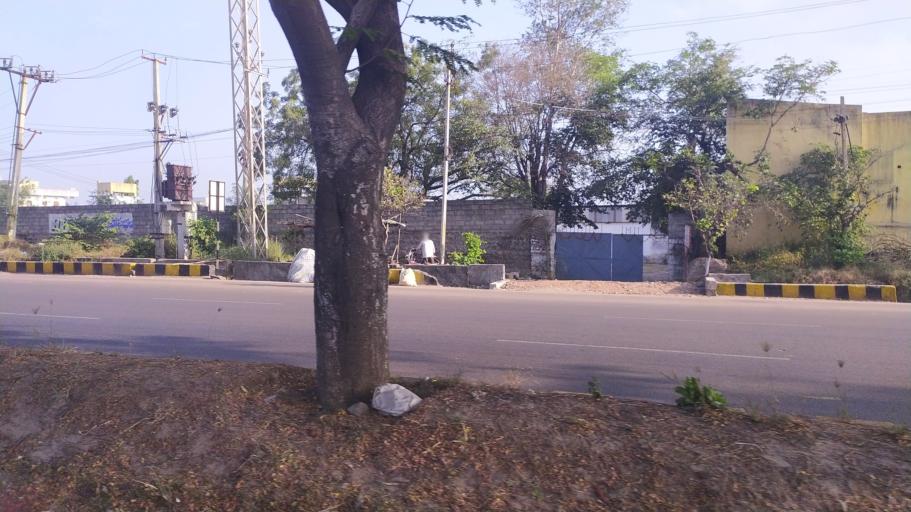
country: IN
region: Telangana
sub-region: Rangareddi
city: Balapur
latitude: 17.3188
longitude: 78.4361
